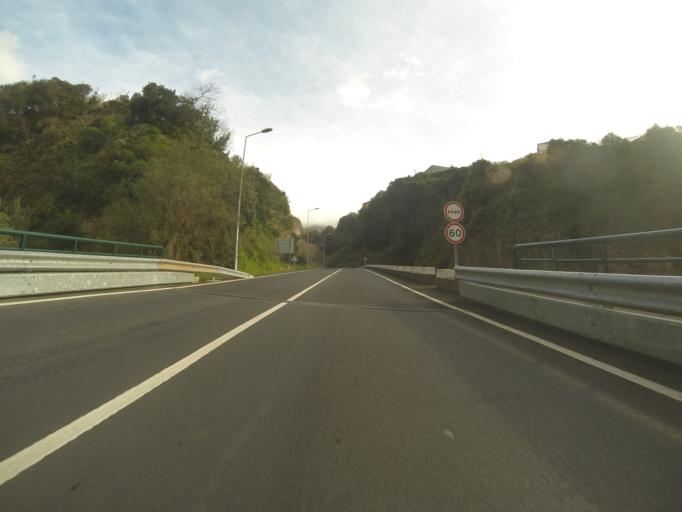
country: PT
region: Madeira
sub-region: Sao Vicente
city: Sao Vicente
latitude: 32.7915
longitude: -17.0342
